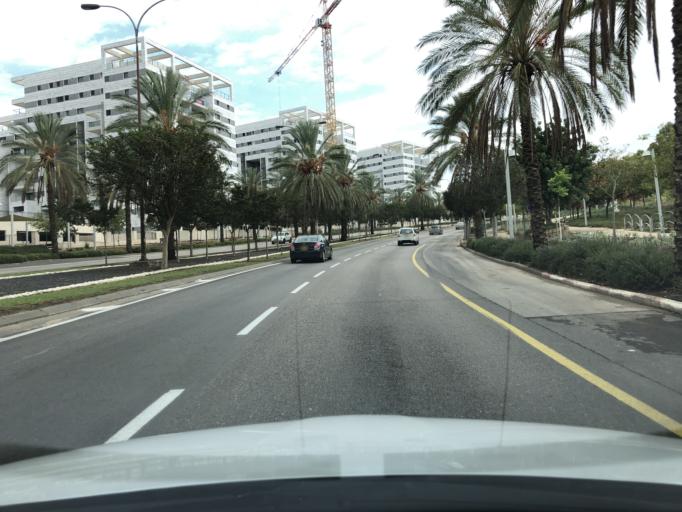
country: IL
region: Central District
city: Modiin
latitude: 31.9091
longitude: 35.0069
